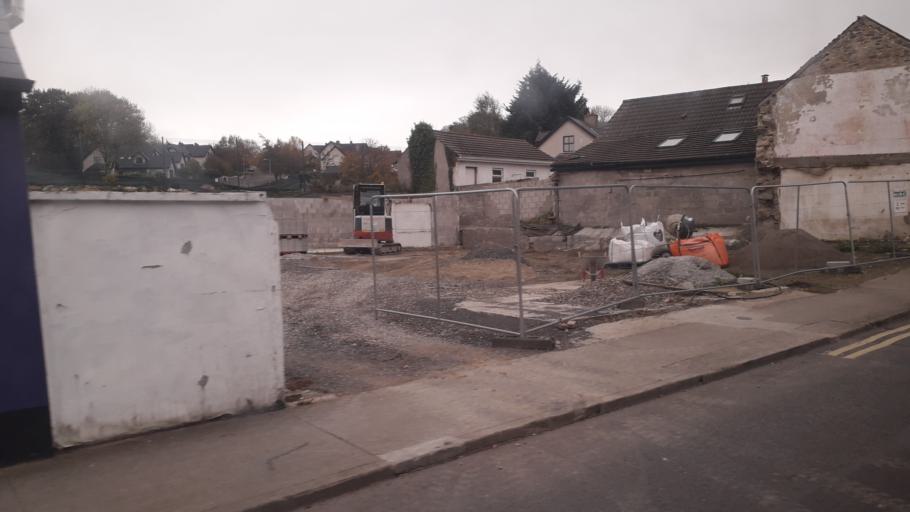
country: IE
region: Munster
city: Ballina
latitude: 52.8080
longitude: -8.4368
